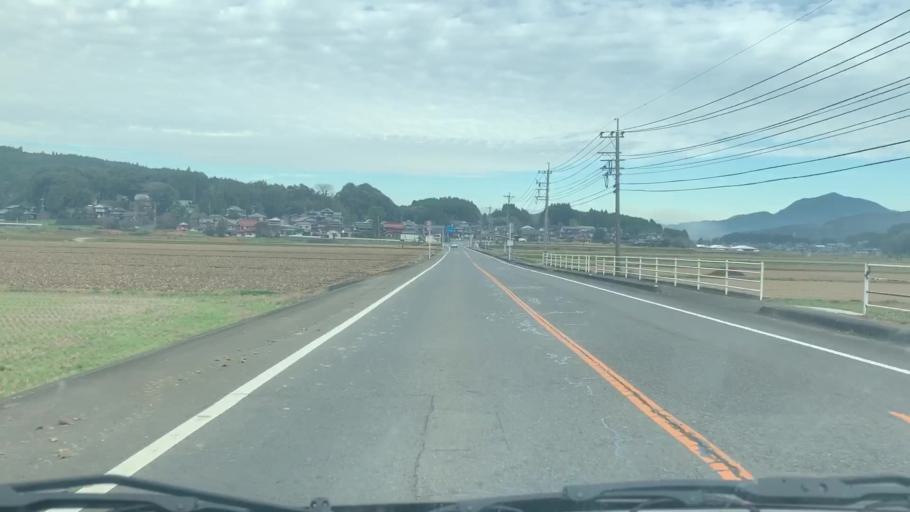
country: JP
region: Saga Prefecture
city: Takeocho-takeo
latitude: 33.2139
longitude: 129.9631
